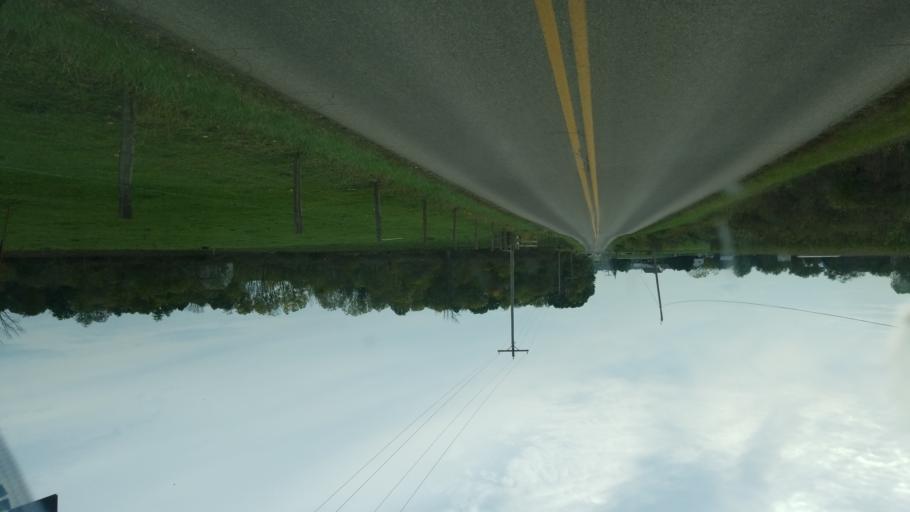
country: US
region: Ohio
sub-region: Holmes County
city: Millersburg
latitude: 40.5871
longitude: -81.8168
